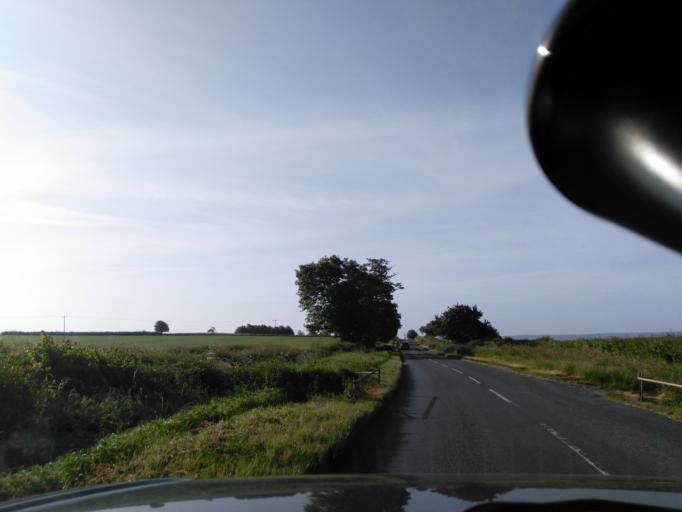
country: GB
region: England
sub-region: Wiltshire
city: Seend
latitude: 51.3402
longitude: -2.0835
